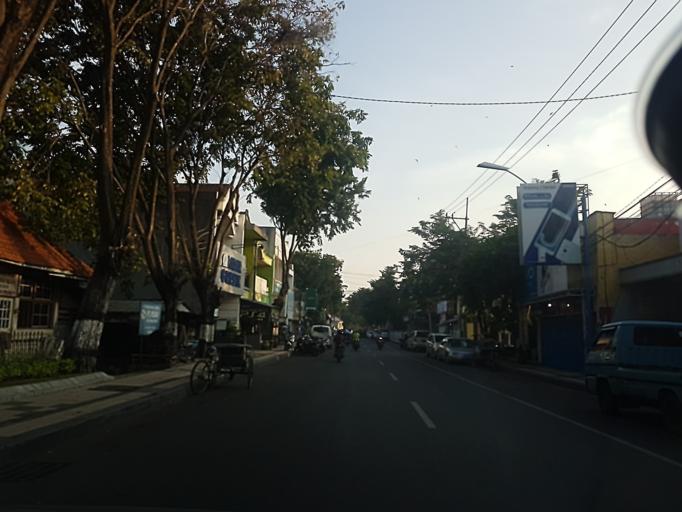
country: ID
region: East Java
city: Gresik
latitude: -7.1612
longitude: 112.6552
